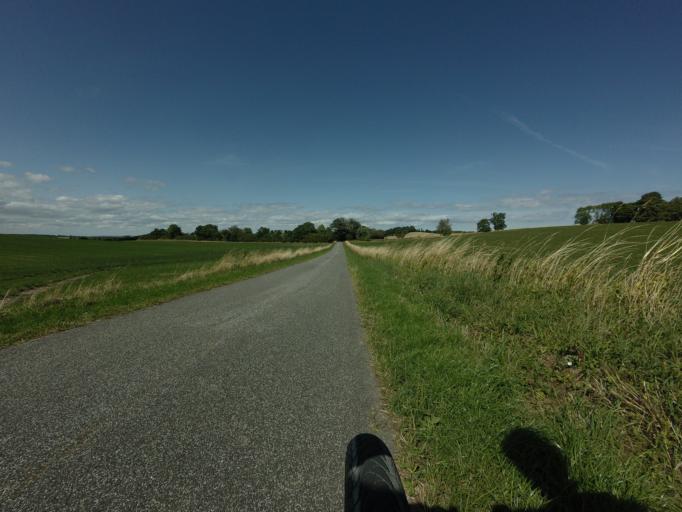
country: DK
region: Zealand
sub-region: Vordingborg Kommune
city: Stege
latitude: 55.0001
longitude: 12.4768
